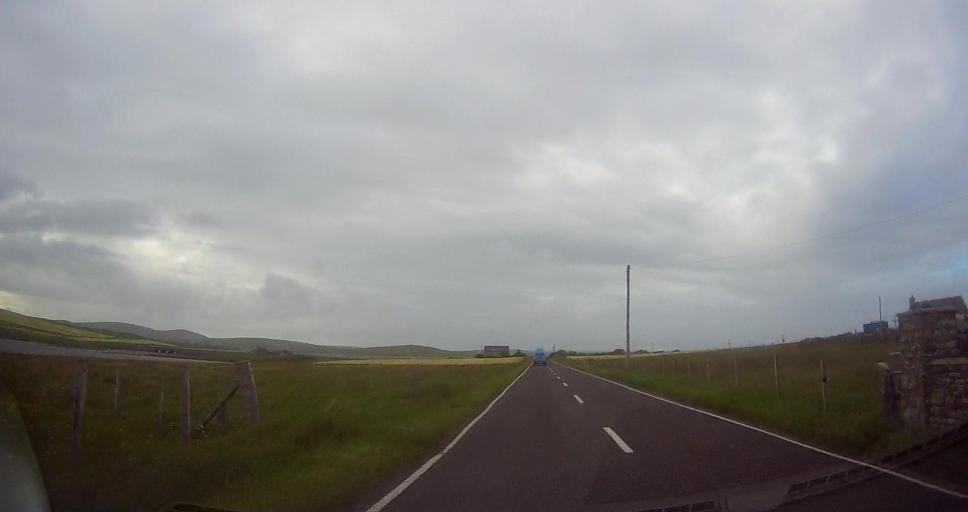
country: GB
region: Scotland
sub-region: Orkney Islands
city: Stromness
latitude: 58.9802
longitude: -3.2447
